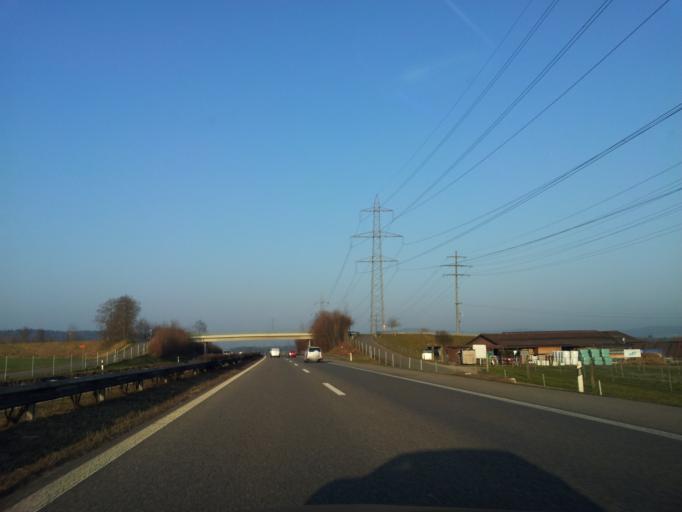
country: CH
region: Aargau
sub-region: Bezirk Rheinfelden
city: Mohlin
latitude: 47.5472
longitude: 7.8446
